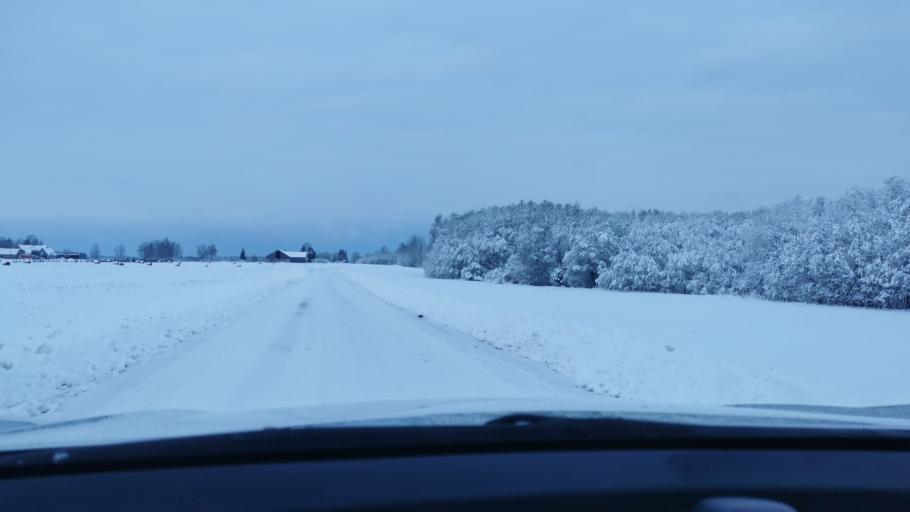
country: EE
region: Laeaene-Virumaa
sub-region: Haljala vald
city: Haljala
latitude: 59.4761
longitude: 26.3646
